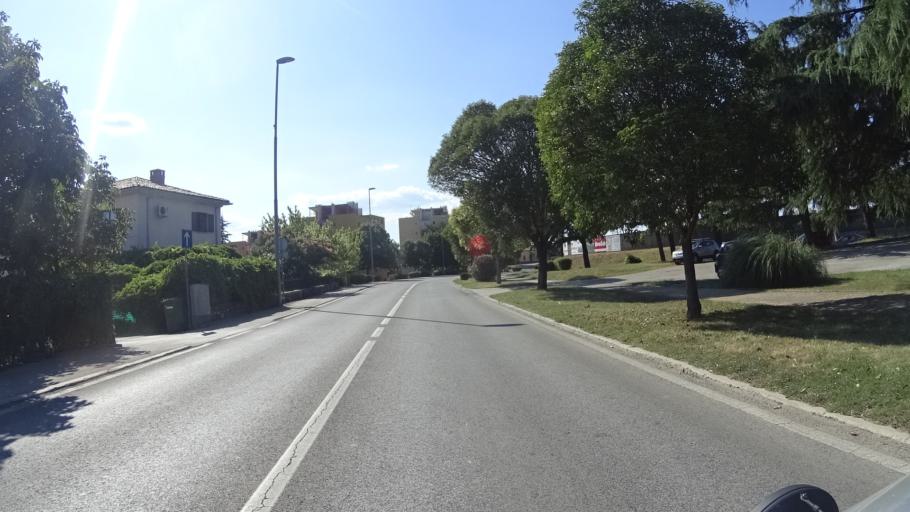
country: HR
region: Istarska
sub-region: Grad Labin
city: Labin
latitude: 45.0952
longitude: 14.1203
